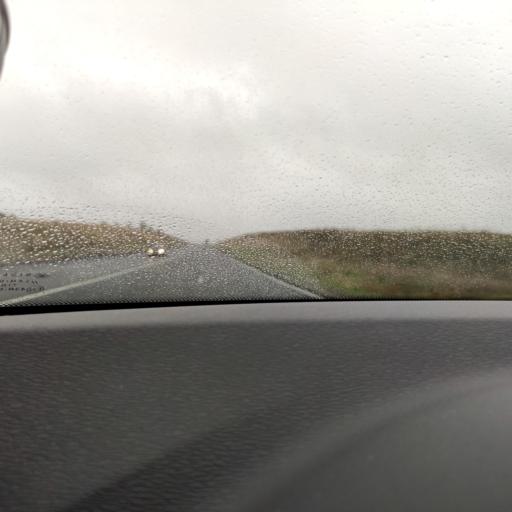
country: RU
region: Samara
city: Yelkhovka
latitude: 53.7360
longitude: 50.2302
